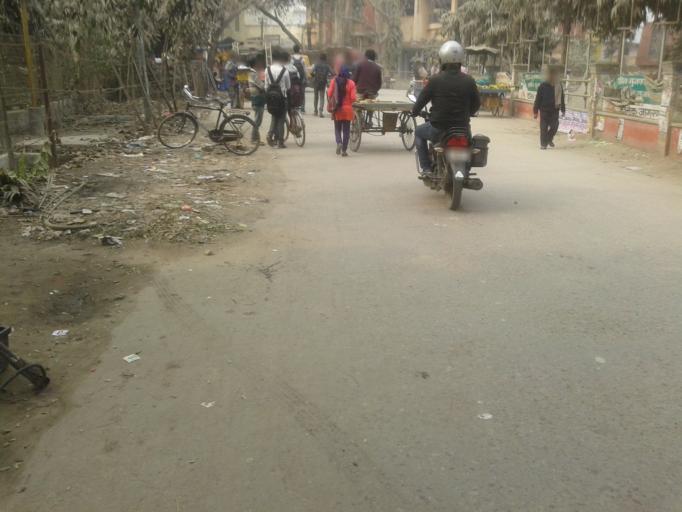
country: IN
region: Bihar
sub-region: Muzaffarpur
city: Muzaffarpur
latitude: 26.1143
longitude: 85.3965
